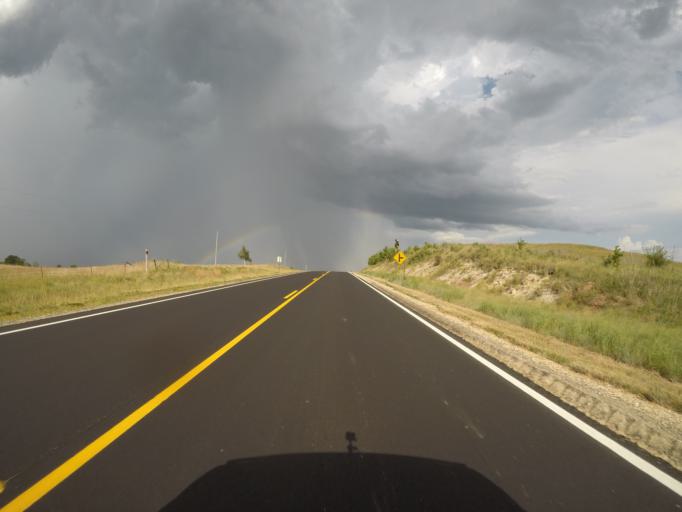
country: US
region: Kansas
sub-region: Marshall County
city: Blue Rapids
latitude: 39.4364
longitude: -96.7761
